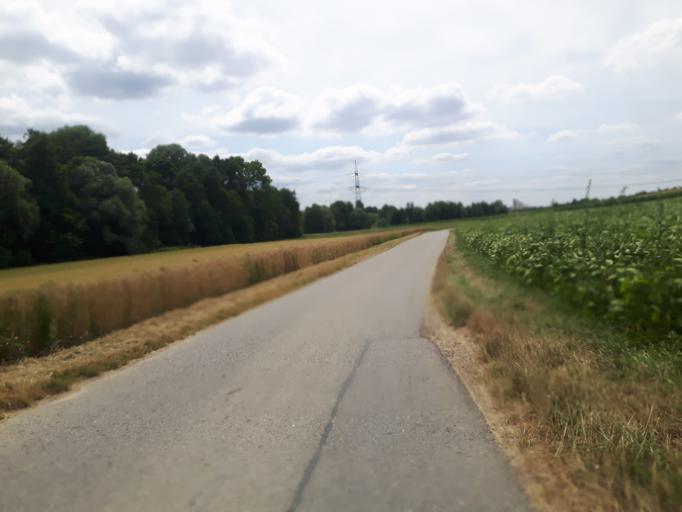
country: DE
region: Baden-Wuerttemberg
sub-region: Regierungsbezirk Stuttgart
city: Eppingen
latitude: 49.1501
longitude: 8.9349
